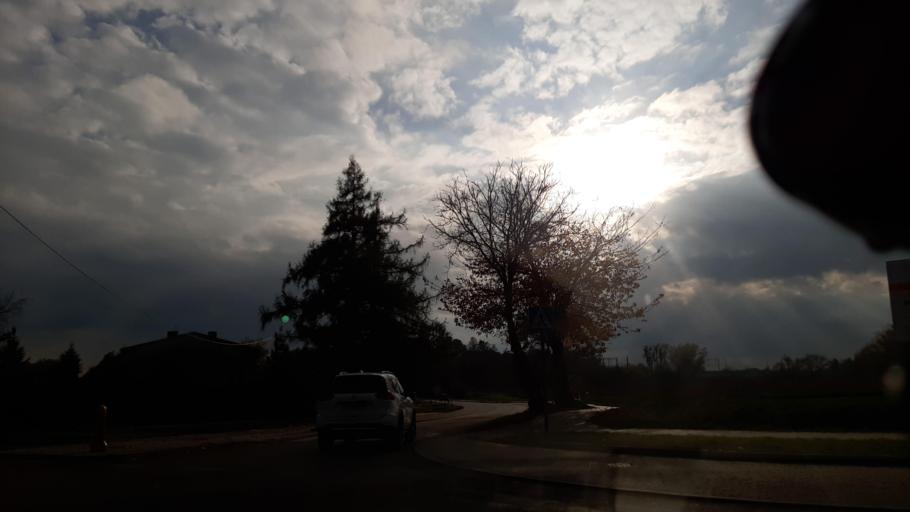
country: PL
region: Lublin Voivodeship
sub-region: Powiat pulawski
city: Naleczow
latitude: 51.3197
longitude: 22.2242
